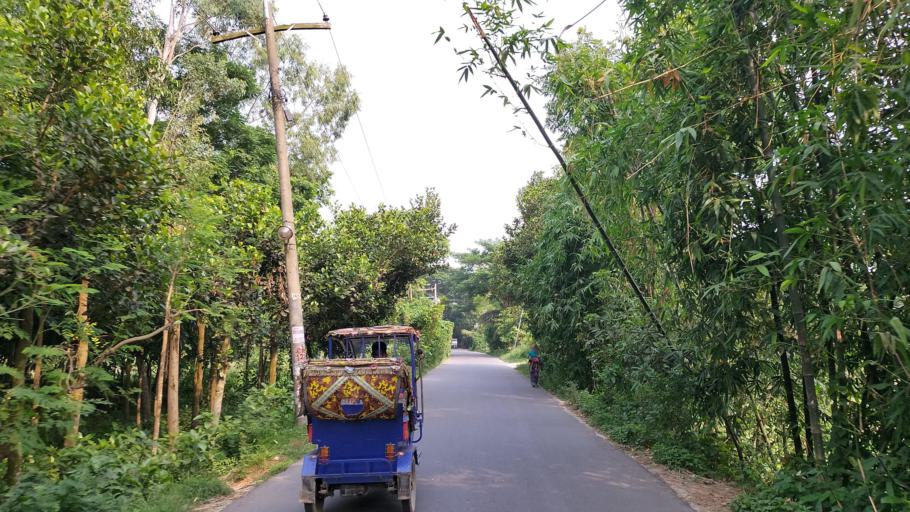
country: BD
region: Dhaka
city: Azimpur
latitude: 23.6776
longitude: 90.3164
